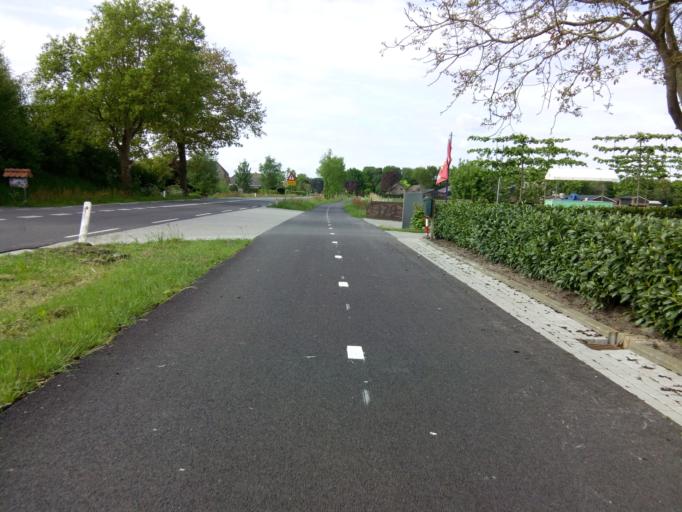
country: NL
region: Gelderland
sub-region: Gemeente Barneveld
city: Terschuur
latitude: 52.1118
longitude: 5.5324
